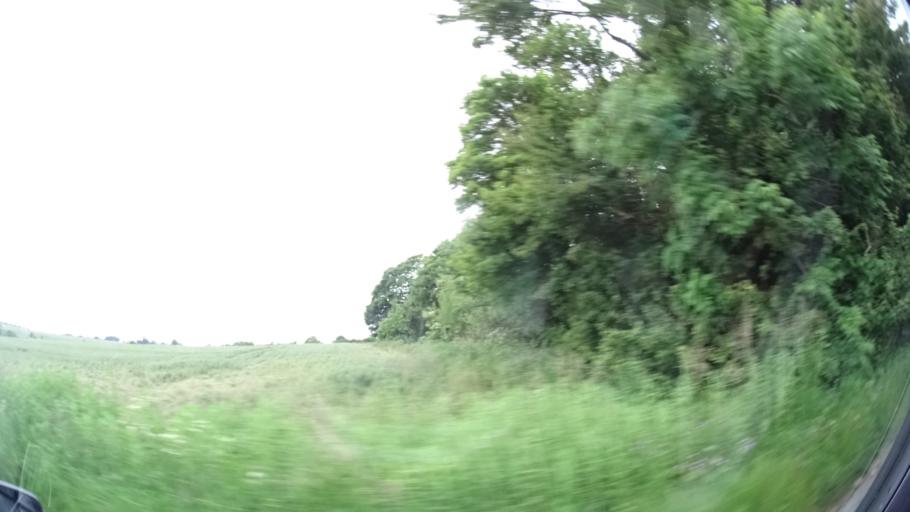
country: DK
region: Central Jutland
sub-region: Arhus Kommune
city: Solbjerg
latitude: 56.0649
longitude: 10.0951
